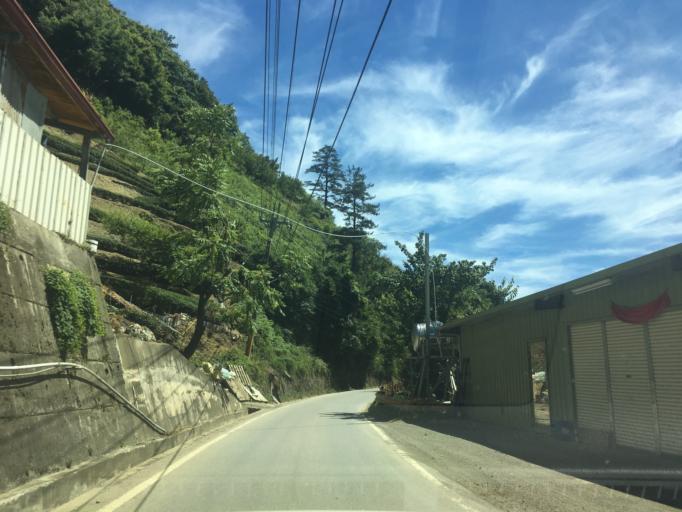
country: TW
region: Taiwan
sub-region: Nantou
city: Puli
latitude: 24.2328
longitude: 121.2536
